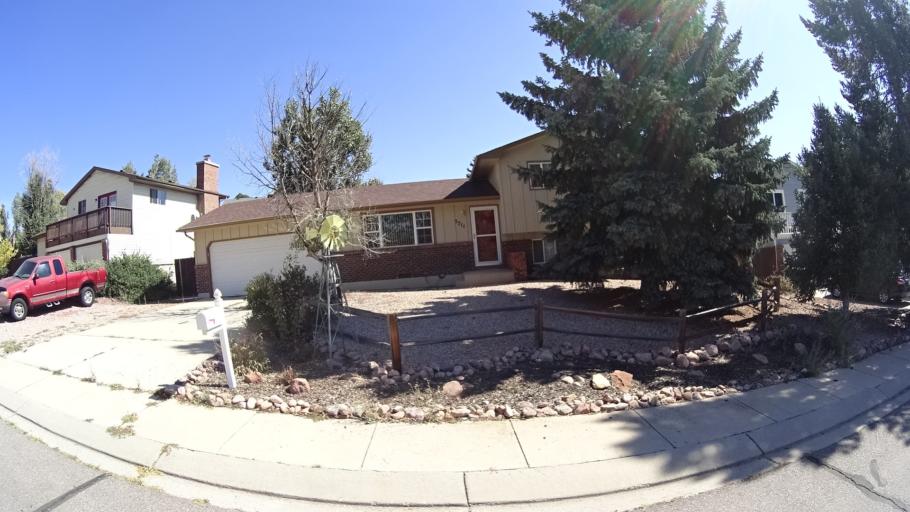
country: US
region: Colorado
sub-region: El Paso County
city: Cimarron Hills
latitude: 38.9154
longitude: -104.7670
